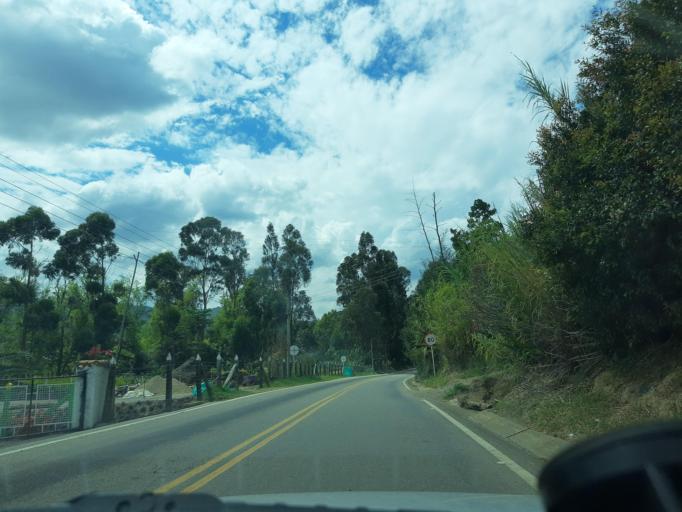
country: CO
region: Boyaca
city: Raquira
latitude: 5.5711
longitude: -73.6549
